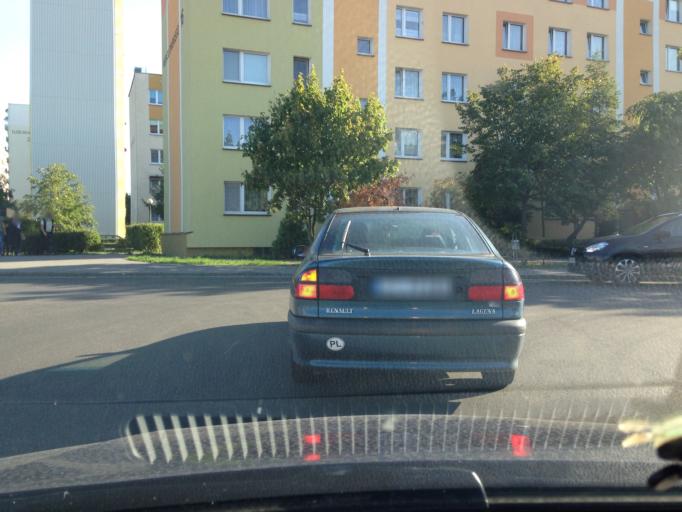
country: PL
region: Kujawsko-Pomorskie
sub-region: Powiat torunski
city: Lubicz Dolny
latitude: 53.0308
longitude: 18.6739
